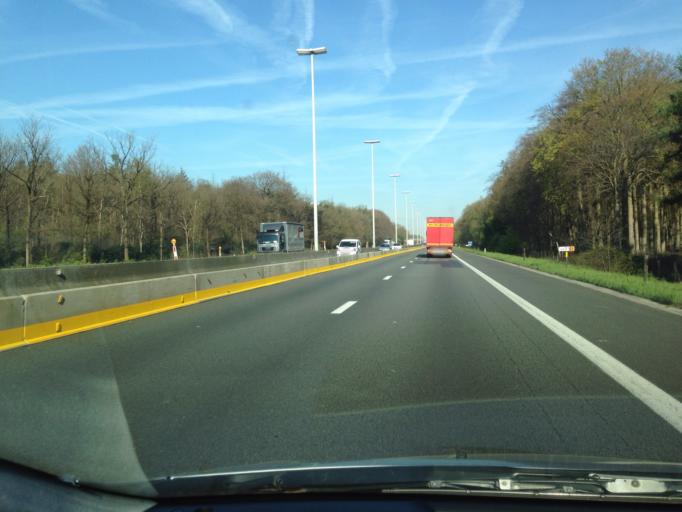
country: BE
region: Flanders
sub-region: Provincie Oost-Vlaanderen
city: Knesselare
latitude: 51.1006
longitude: 3.3862
